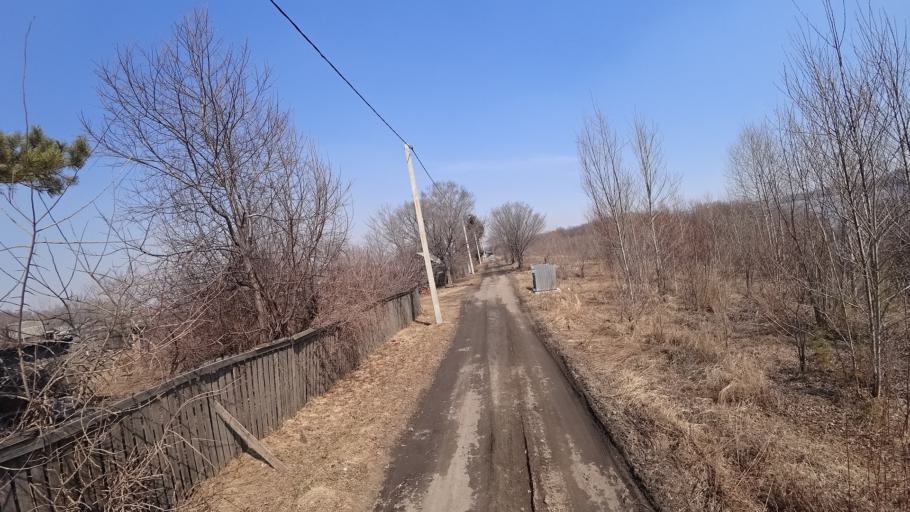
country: RU
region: Amur
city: Novobureyskiy
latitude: 49.7778
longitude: 129.8511
